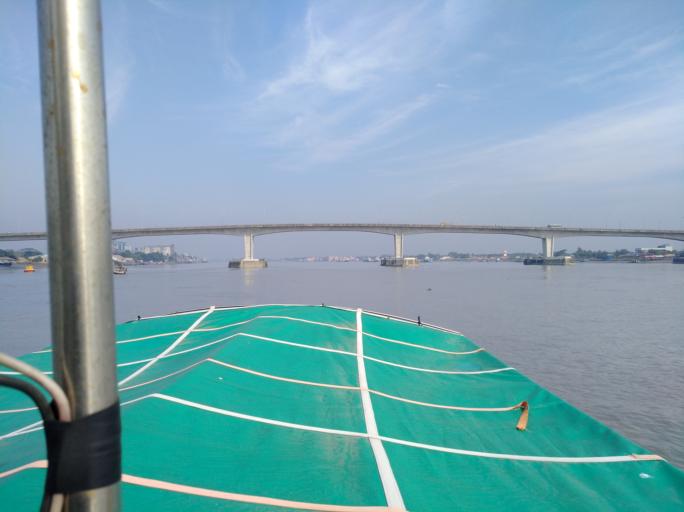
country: BD
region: Khulna
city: Khulna
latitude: 22.7745
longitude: 89.5833
